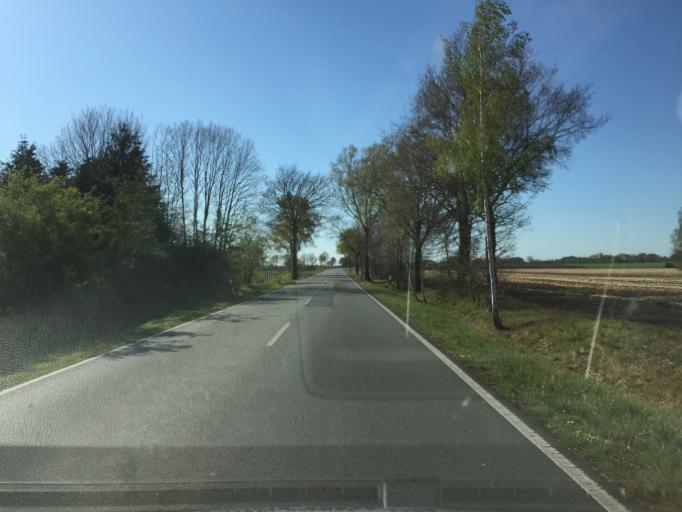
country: DE
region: Lower Saxony
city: Varrel
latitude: 52.6383
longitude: 8.7365
